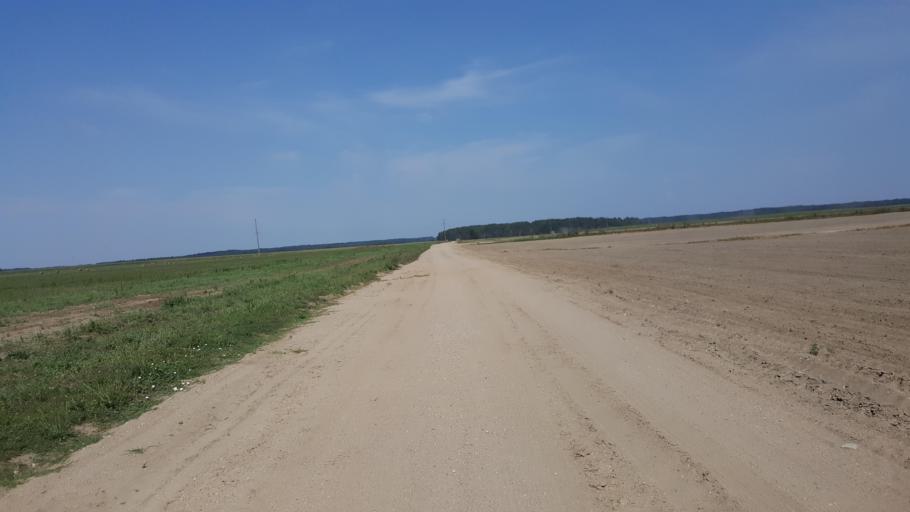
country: BY
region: Brest
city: Kamyanyuki
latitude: 52.4937
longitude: 23.6018
